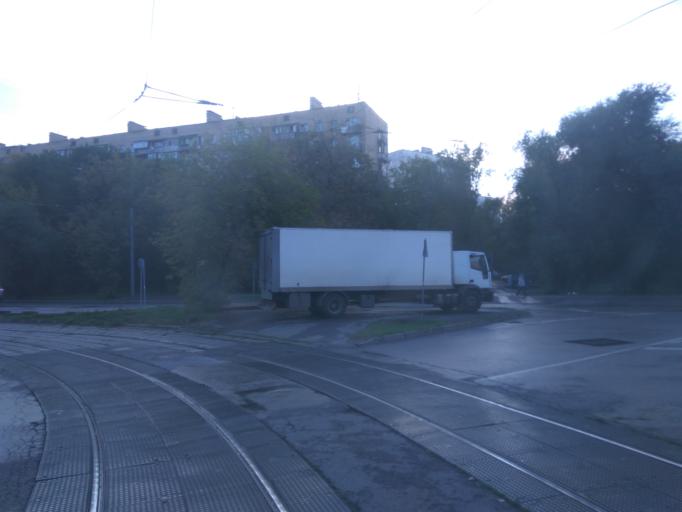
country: RU
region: Moskovskaya
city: Bogorodskoye
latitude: 55.8183
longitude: 37.7215
